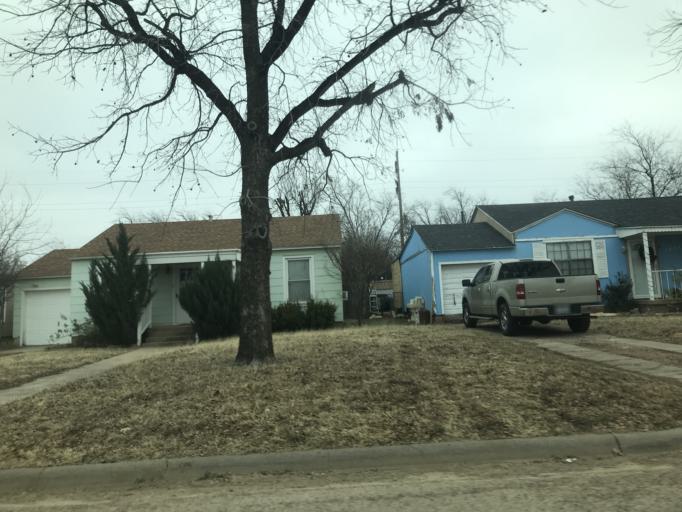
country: US
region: Texas
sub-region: Taylor County
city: Abilene
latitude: 32.4293
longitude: -99.7549
